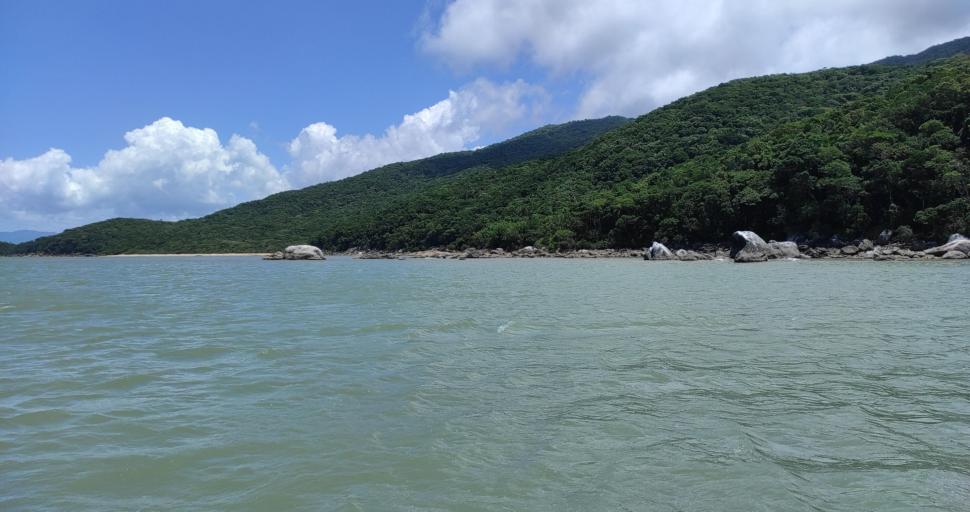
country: BR
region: Santa Catarina
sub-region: Porto Belo
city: Porto Belo
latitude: -27.1998
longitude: -48.5607
